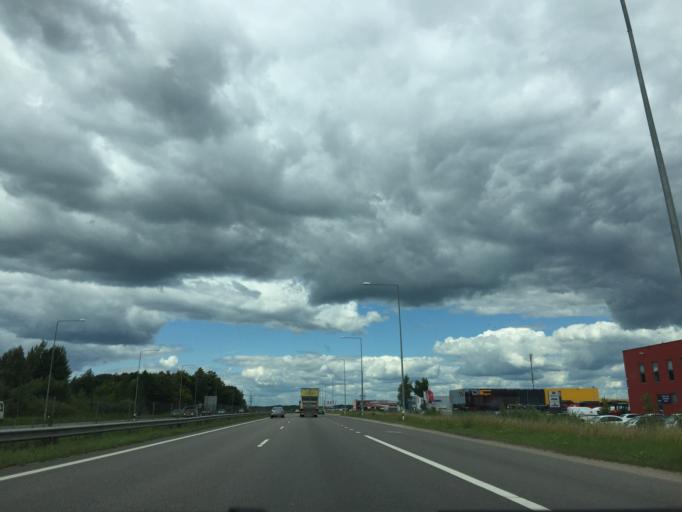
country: LT
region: Kauno apskritis
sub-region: Kaunas
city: Sargenai
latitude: 54.9549
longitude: 23.8691
